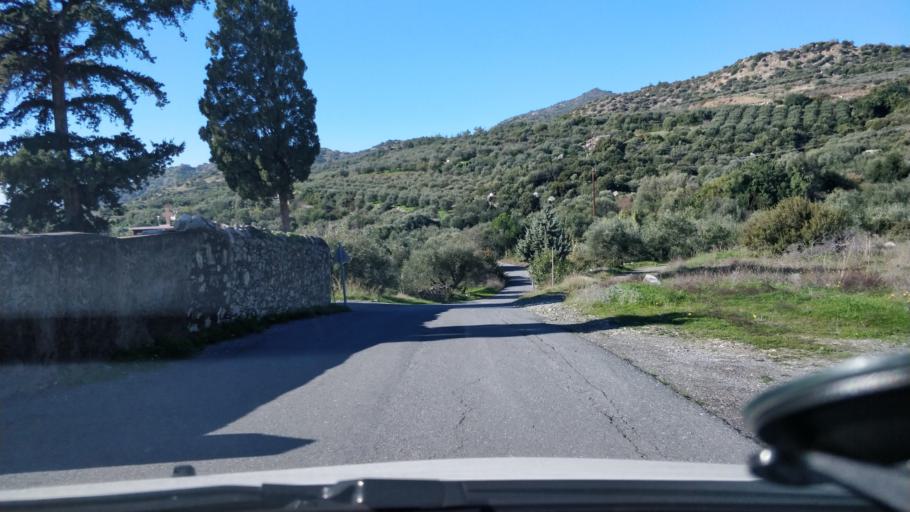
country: GR
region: Crete
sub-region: Nomos Lasithiou
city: Gra Liyia
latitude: 35.0202
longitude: 25.5563
